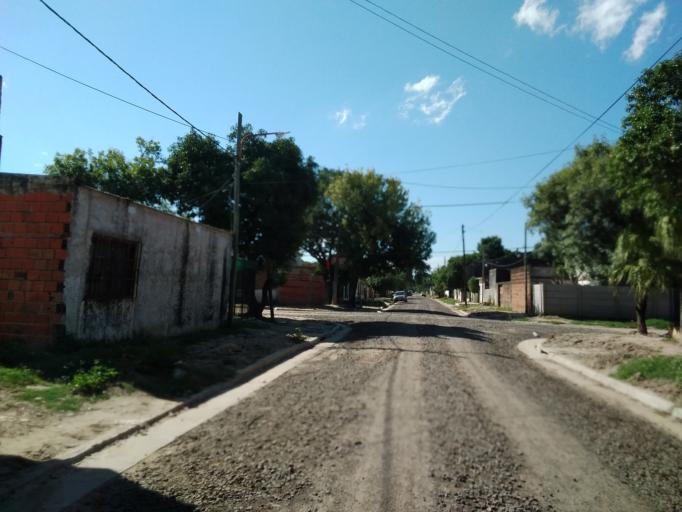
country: AR
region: Corrientes
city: Corrientes
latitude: -27.4852
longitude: -58.8108
